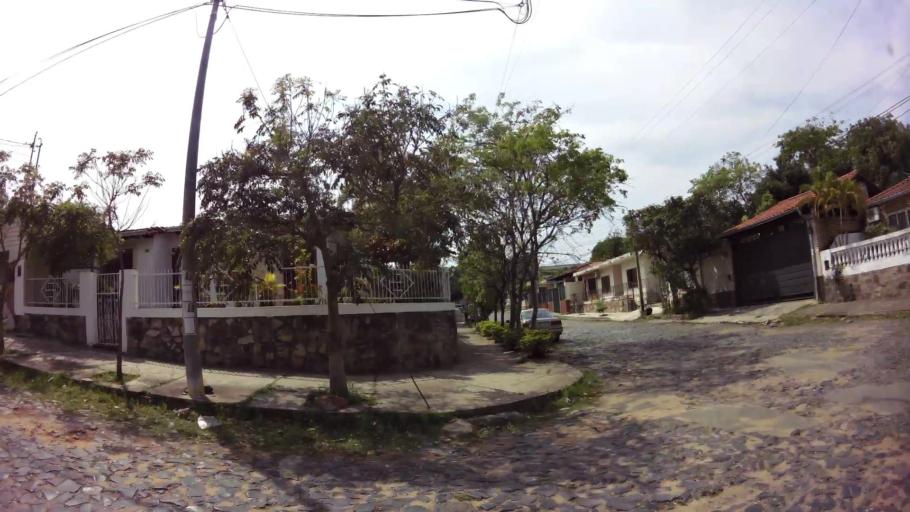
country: PY
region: Asuncion
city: Asuncion
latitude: -25.2652
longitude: -57.5835
